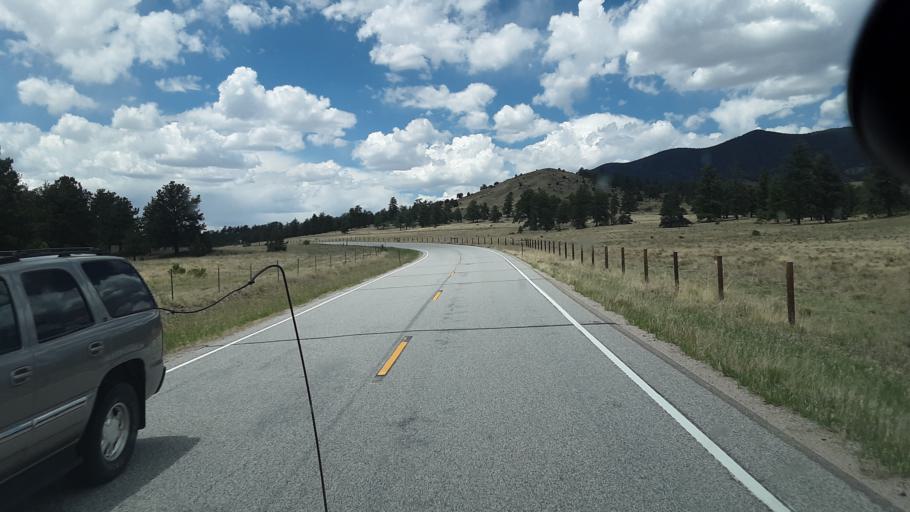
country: US
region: Colorado
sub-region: Teller County
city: Cripple Creek
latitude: 38.7792
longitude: -105.5694
